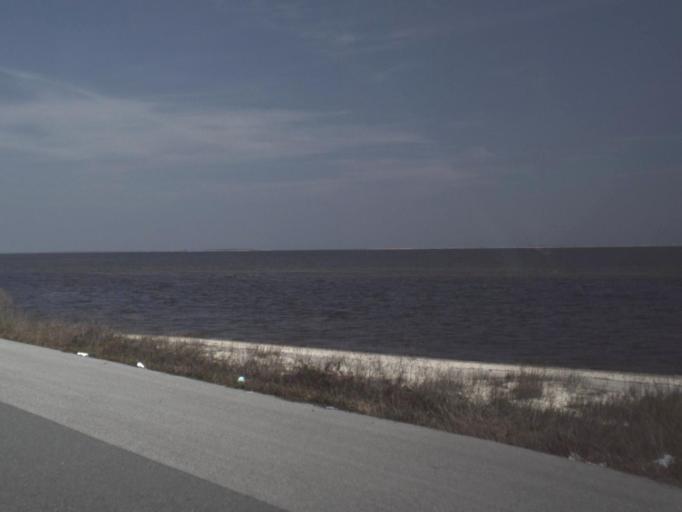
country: US
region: Florida
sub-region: Franklin County
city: Eastpoint
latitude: 29.7820
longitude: -84.7751
